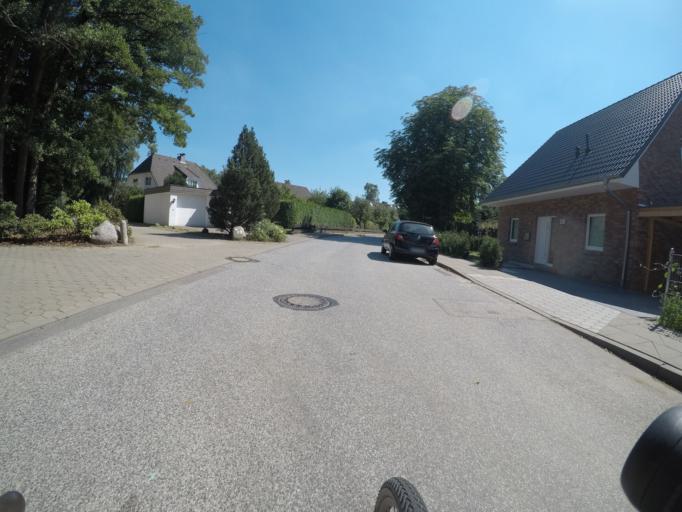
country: DE
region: Schleswig-Holstein
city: Oststeinbek
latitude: 53.5117
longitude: 10.1672
